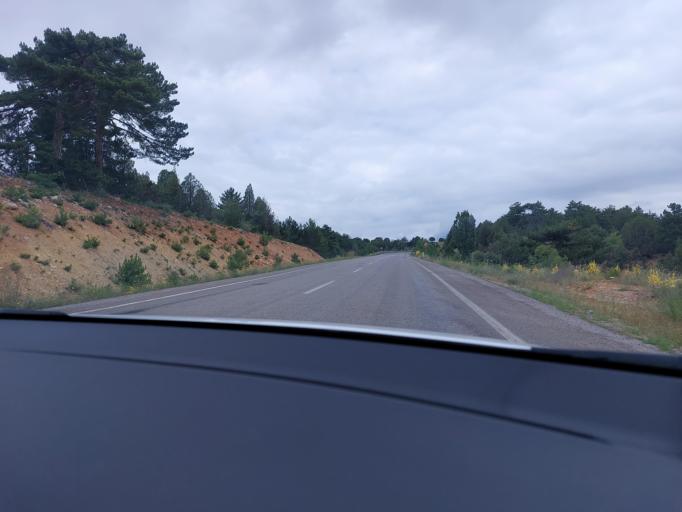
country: TR
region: Konya
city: Doganbey
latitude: 37.8915
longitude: 31.8195
